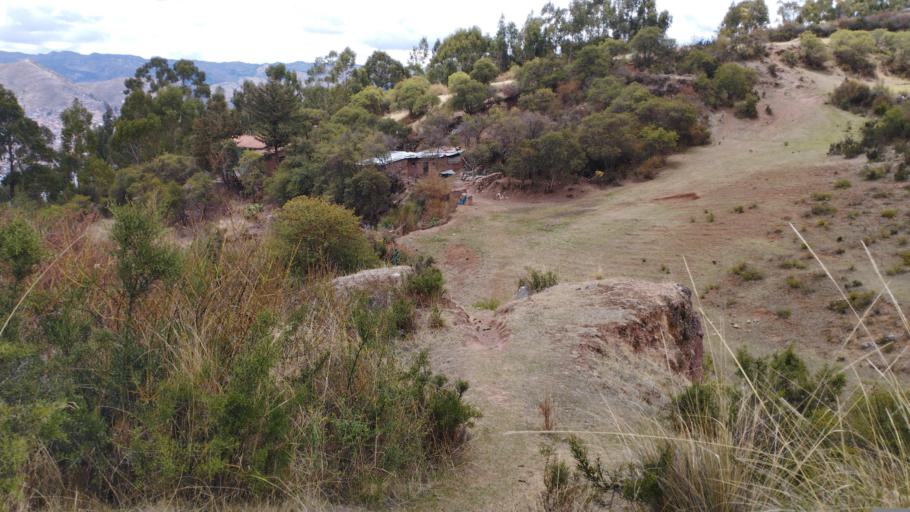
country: PE
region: Cusco
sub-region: Provincia de Cusco
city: Cusco
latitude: -13.5187
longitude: -71.9402
